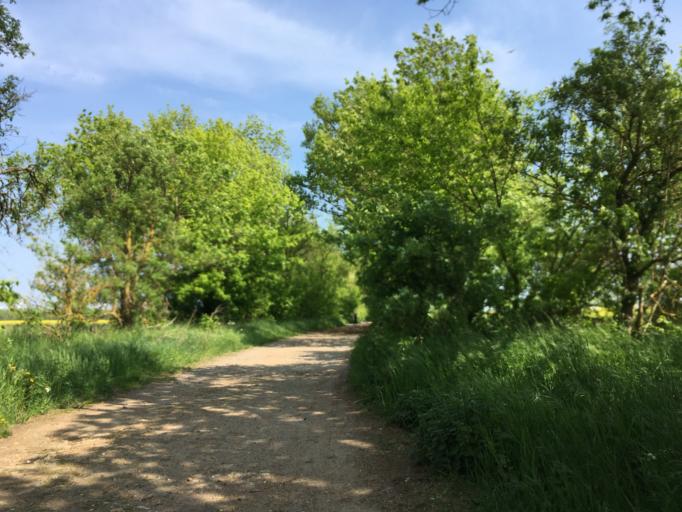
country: DE
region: Brandenburg
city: Altlandsberg
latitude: 52.5876
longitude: 13.7264
